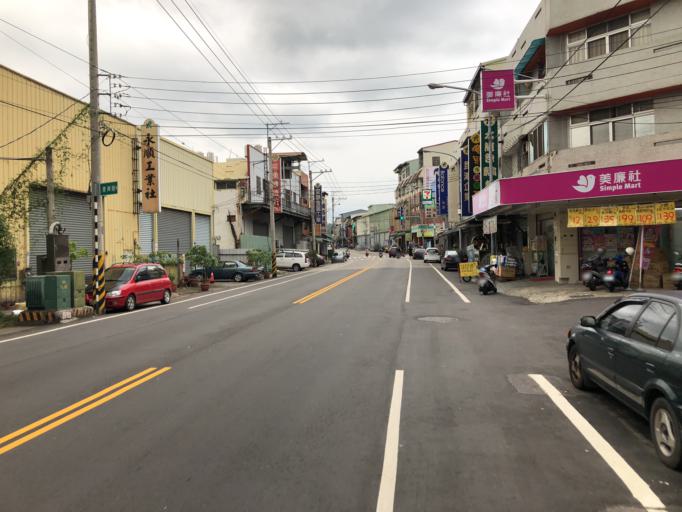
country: TW
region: Taiwan
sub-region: Taichung City
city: Taichung
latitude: 24.1206
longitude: 120.7339
